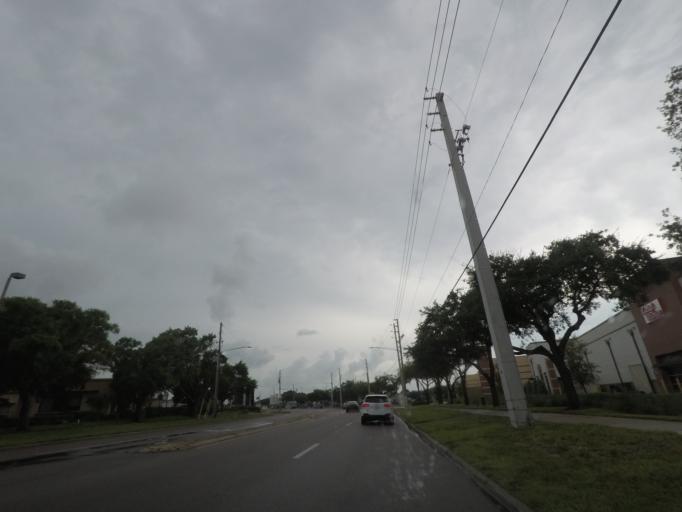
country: US
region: Florida
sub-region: Pinellas County
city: Kenneth City
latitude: 27.7914
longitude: -82.7305
